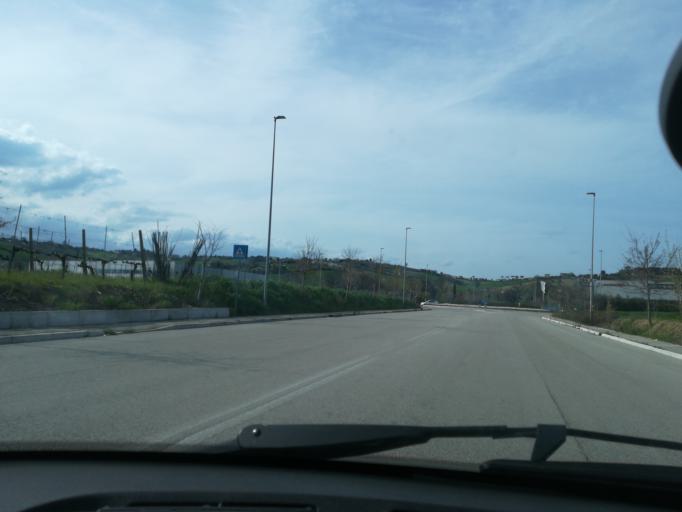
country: IT
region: The Marches
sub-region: Provincia di Macerata
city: Piediripa
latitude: 43.2819
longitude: 13.4972
